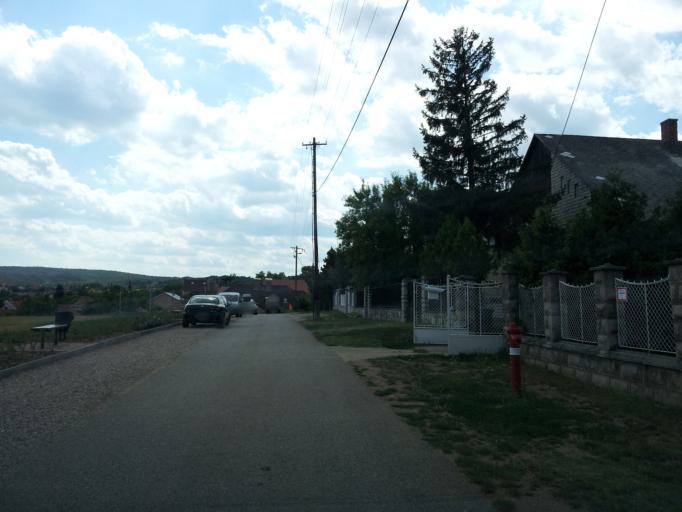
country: HU
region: Veszprem
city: Balatonalmadi
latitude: 47.0475
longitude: 18.0084
